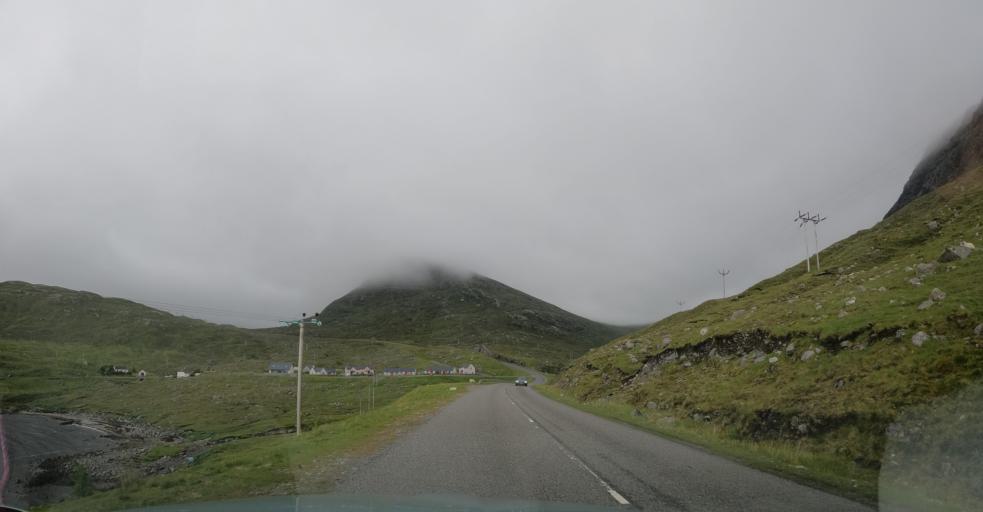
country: GB
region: Scotland
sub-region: Eilean Siar
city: Harris
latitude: 57.9272
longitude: -6.8406
